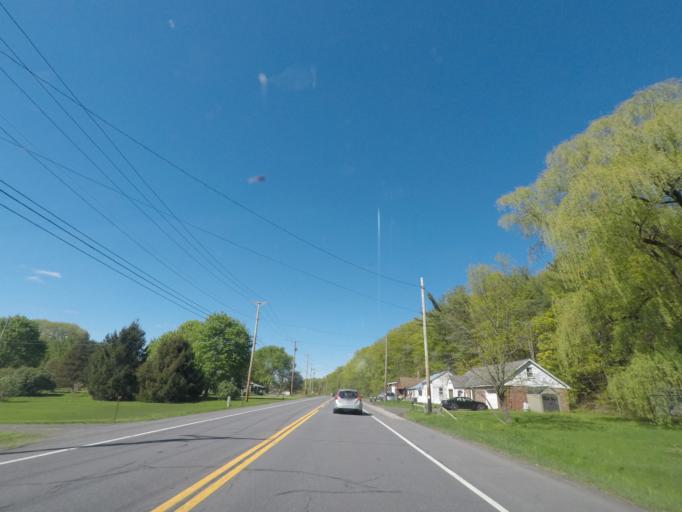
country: US
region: New York
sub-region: Albany County
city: Ravena
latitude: 42.4271
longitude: -73.8168
